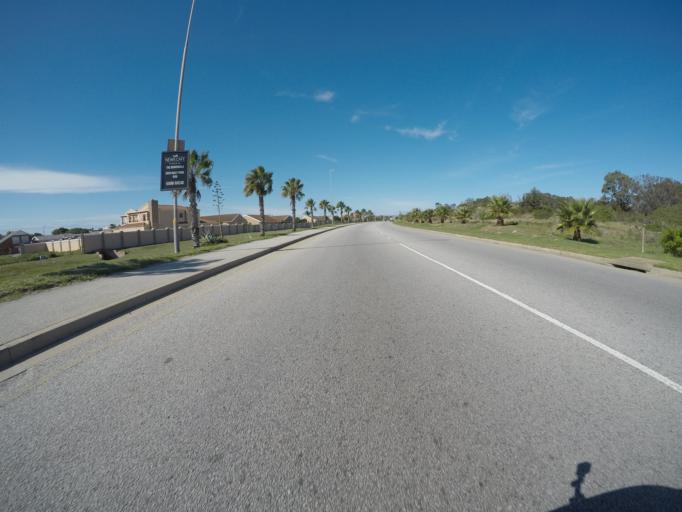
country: ZA
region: Eastern Cape
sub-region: Nelson Mandela Bay Metropolitan Municipality
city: Port Elizabeth
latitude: -33.9884
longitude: 25.6461
